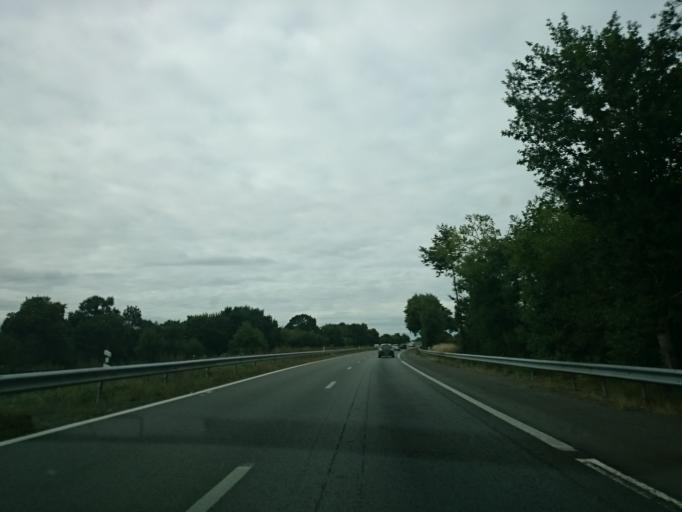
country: FR
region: Brittany
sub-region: Departement d'Ille-et-Vilaine
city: Grand-Fougeray
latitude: 47.7277
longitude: -1.7120
